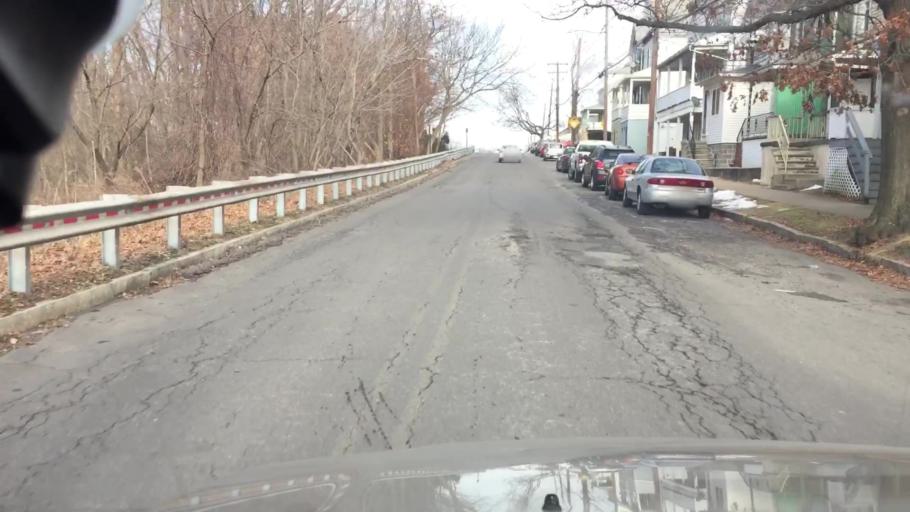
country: US
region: Pennsylvania
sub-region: Luzerne County
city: Wilkes-Barre
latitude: 41.2334
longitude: -75.8989
